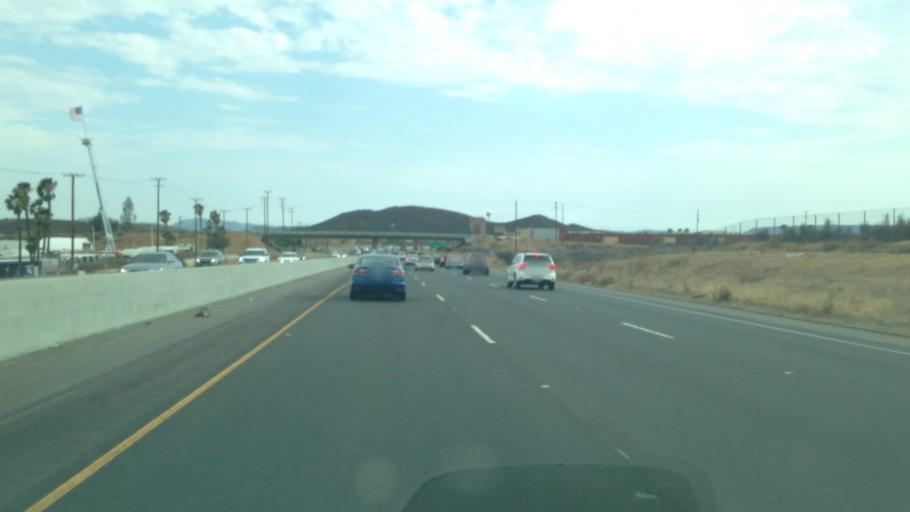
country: US
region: California
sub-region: Riverside County
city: Murrieta Hot Springs
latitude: 33.6087
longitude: -117.1714
